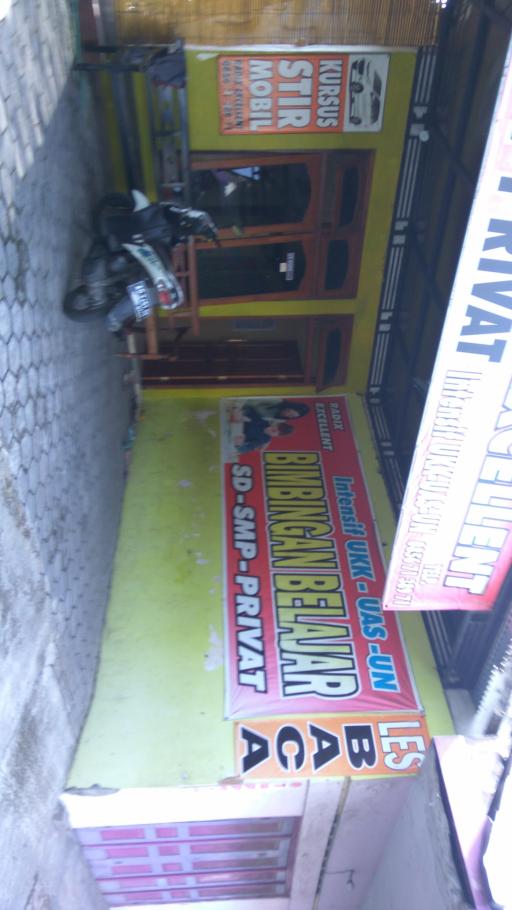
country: ID
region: Central Java
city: Ngemplak
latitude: -7.5532
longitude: 110.6743
